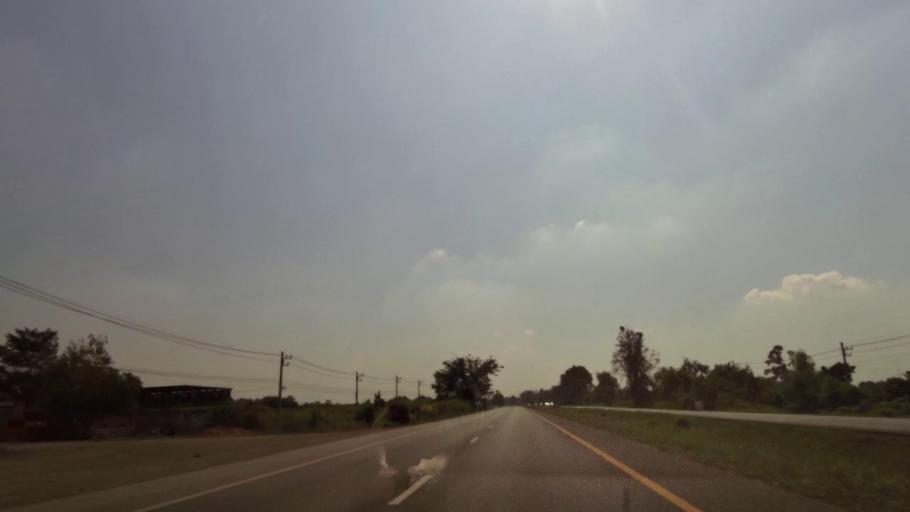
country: TH
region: Phichit
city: Bueng Na Rang
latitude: 16.2472
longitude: 100.1260
